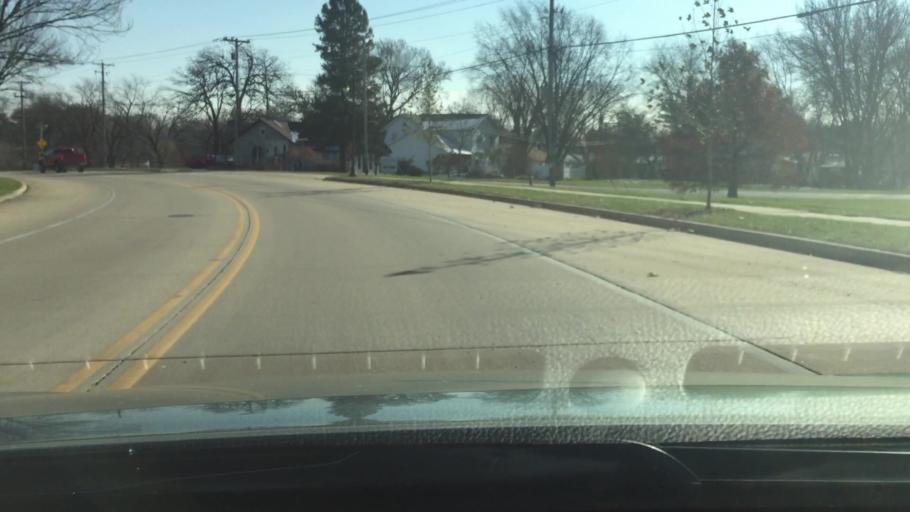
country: US
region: Wisconsin
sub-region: Jefferson County
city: Cambridge
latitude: 43.0049
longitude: -89.0222
